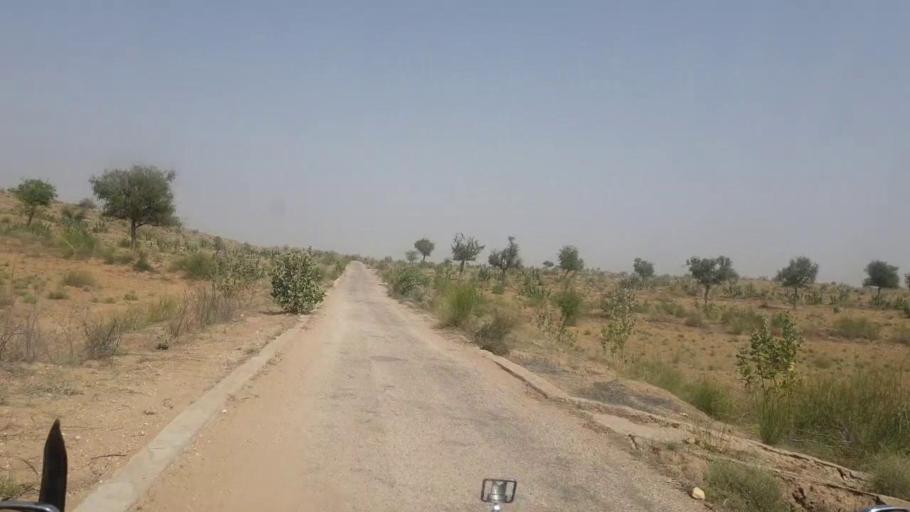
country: PK
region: Sindh
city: Islamkot
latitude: 25.1717
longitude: 70.2012
